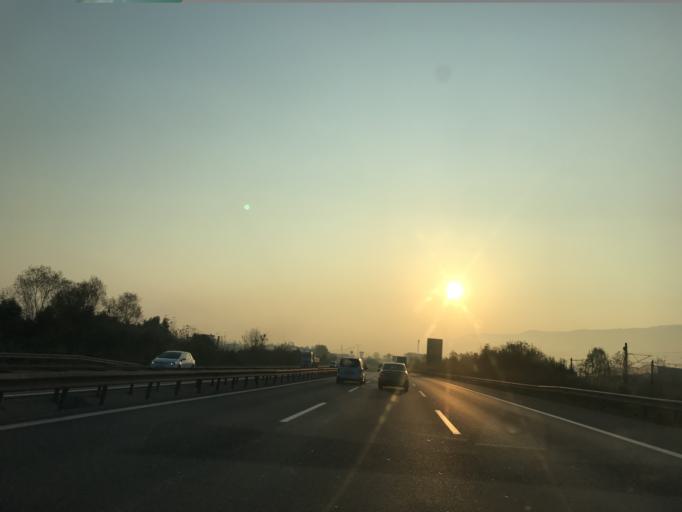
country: TR
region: Kocaeli
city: Derbent
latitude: 40.7313
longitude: 30.0580
